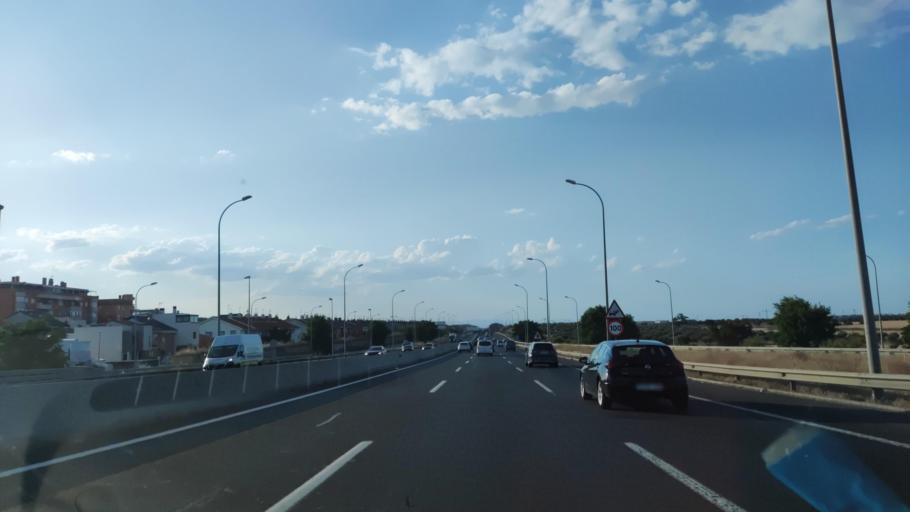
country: ES
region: Madrid
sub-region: Provincia de Madrid
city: Valdemoro
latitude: 40.1785
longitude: -3.6686
